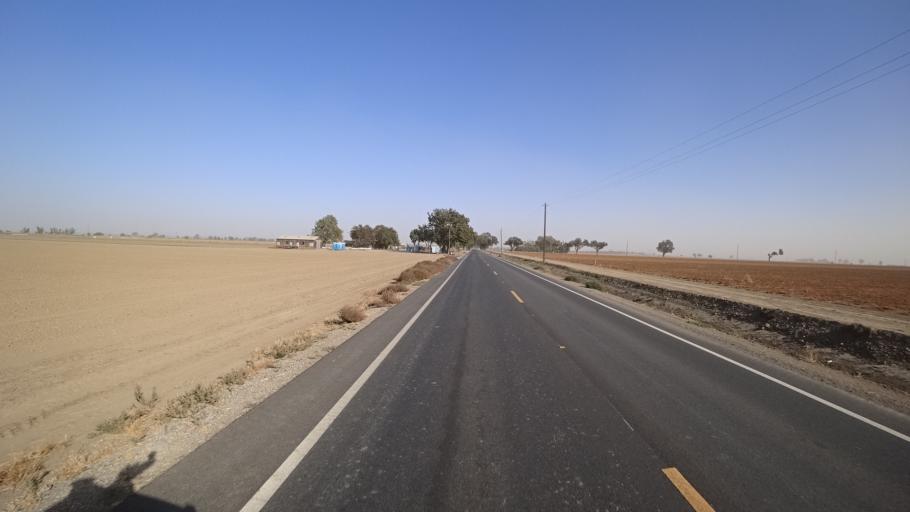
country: US
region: California
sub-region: Yolo County
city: Woodland
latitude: 38.7931
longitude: -121.7687
